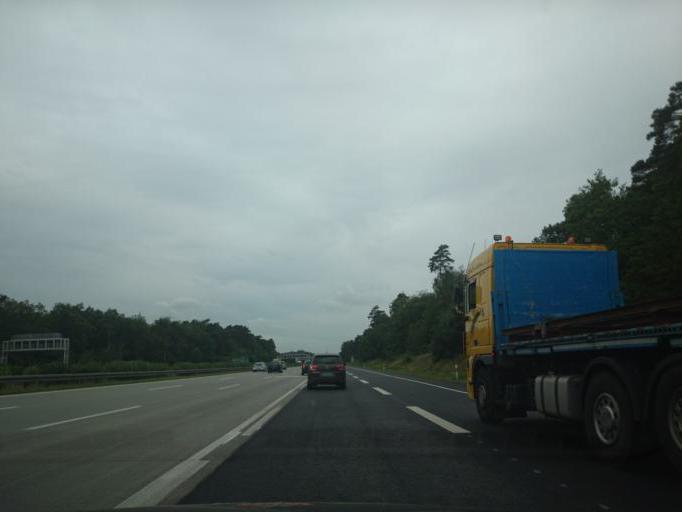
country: DE
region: Brandenburg
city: Schulzendorf
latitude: 52.3190
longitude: 13.5489
